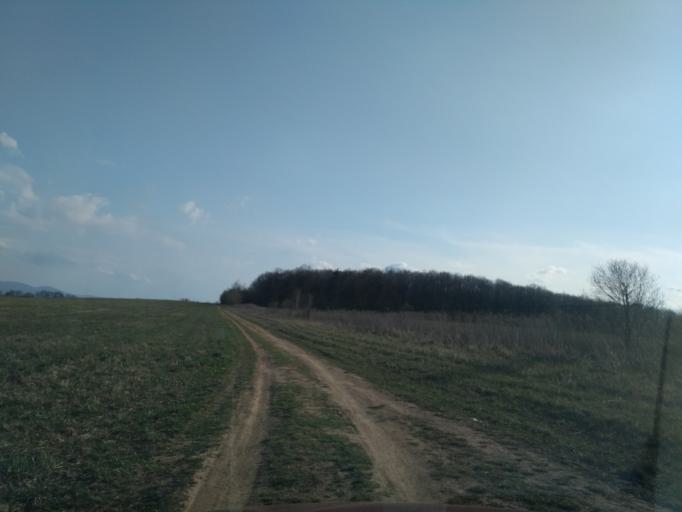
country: SK
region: Kosicky
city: Kosice
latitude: 48.6827
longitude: 21.1811
